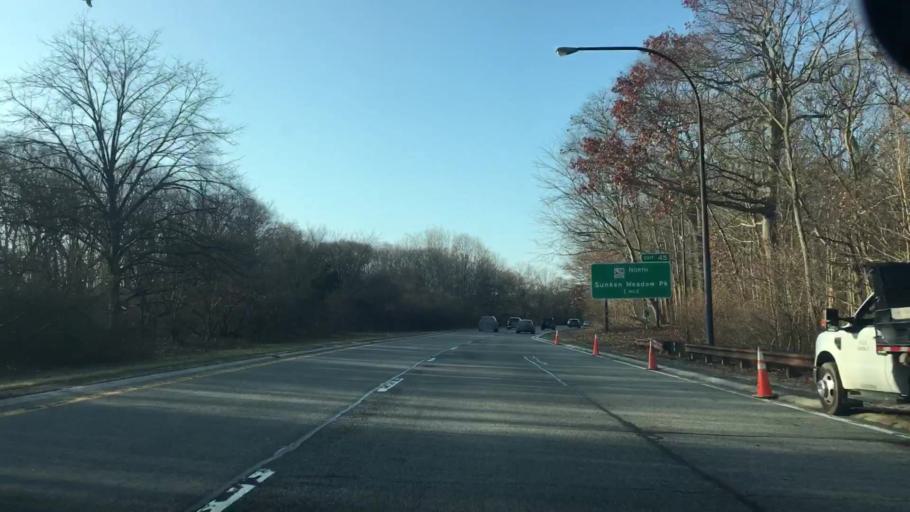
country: US
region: New York
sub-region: Suffolk County
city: Commack
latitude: 40.8201
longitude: -73.2672
